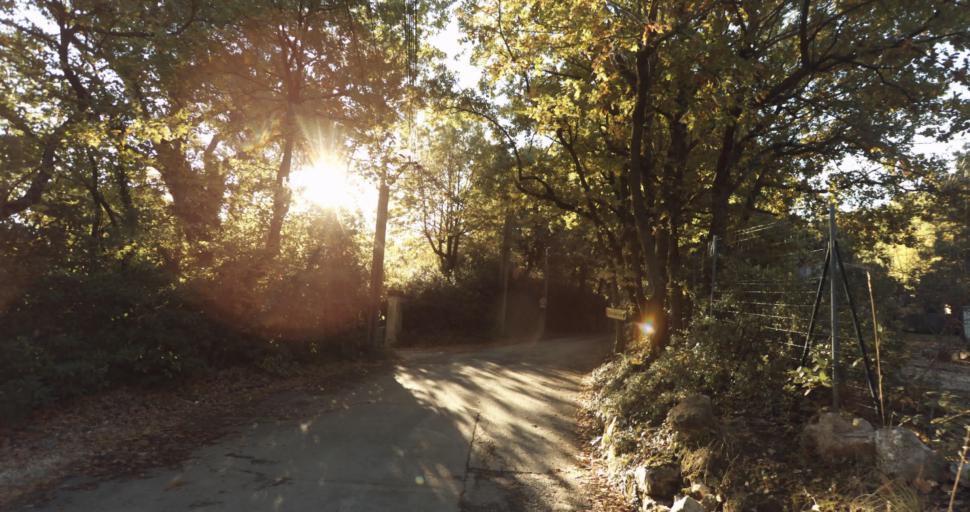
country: FR
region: Provence-Alpes-Cote d'Azur
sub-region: Departement des Bouches-du-Rhone
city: Venelles
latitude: 43.6096
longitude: 5.4797
